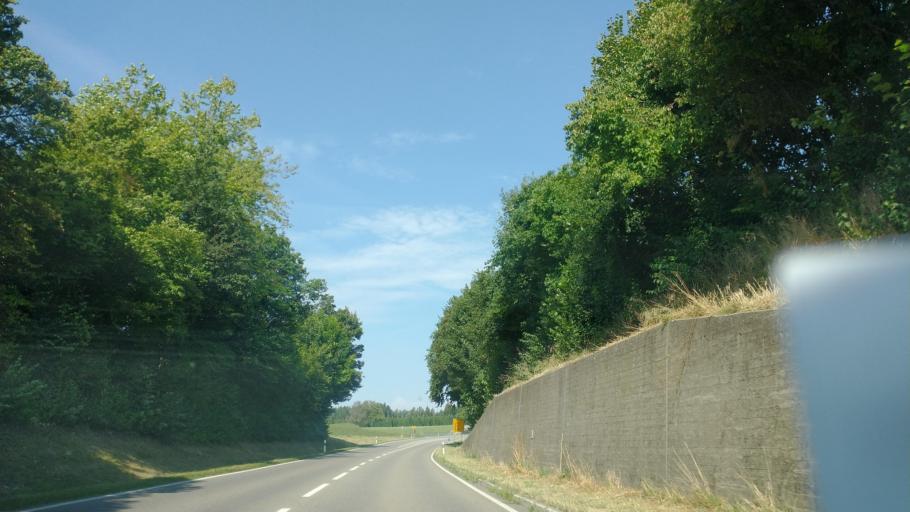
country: DE
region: Baden-Wuerttemberg
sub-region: Tuebingen Region
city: Neukirch
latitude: 47.6566
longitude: 9.6859
